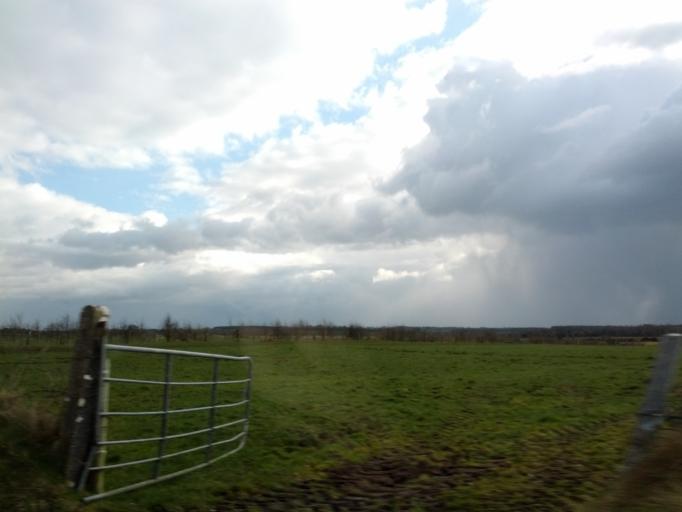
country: IE
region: Connaught
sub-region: County Galway
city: Athenry
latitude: 53.4324
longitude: -8.6597
